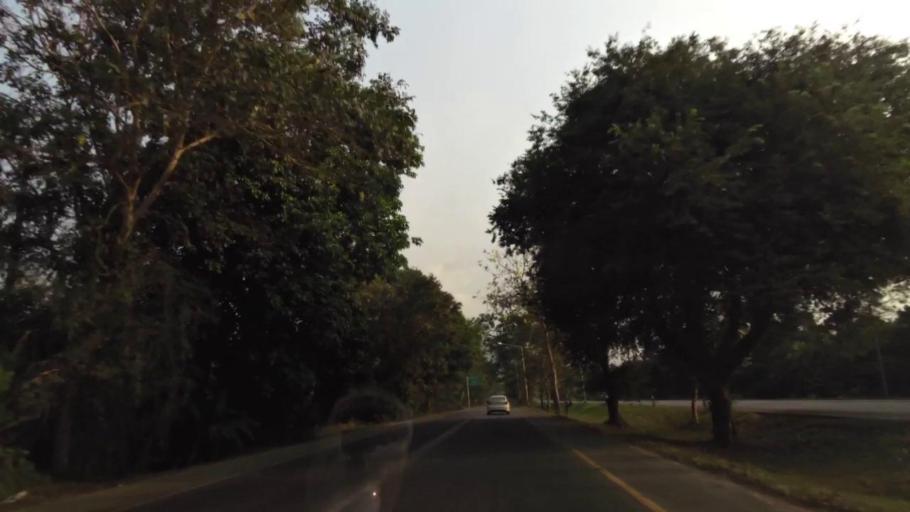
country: TH
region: Chanthaburi
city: Chanthaburi
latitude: 12.5870
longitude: 102.1558
